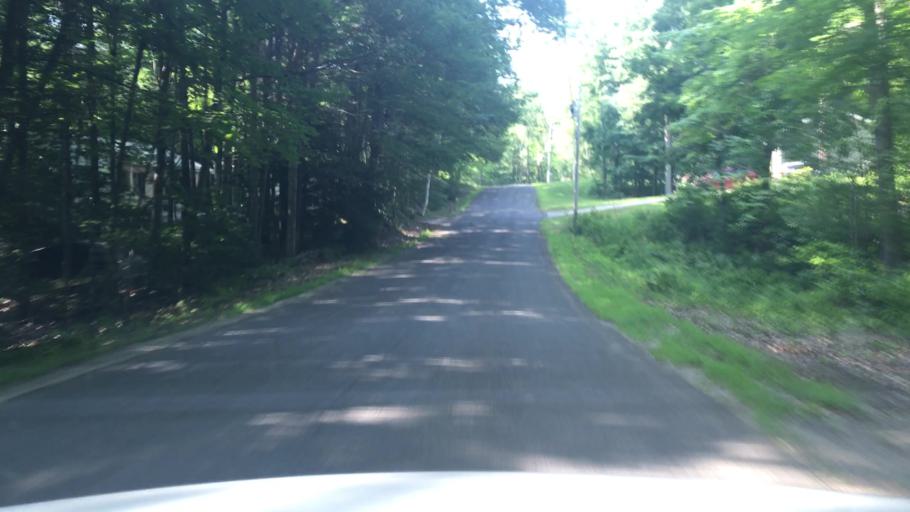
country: US
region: Maine
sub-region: Androscoggin County
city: Greene
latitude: 44.2366
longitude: -70.1057
